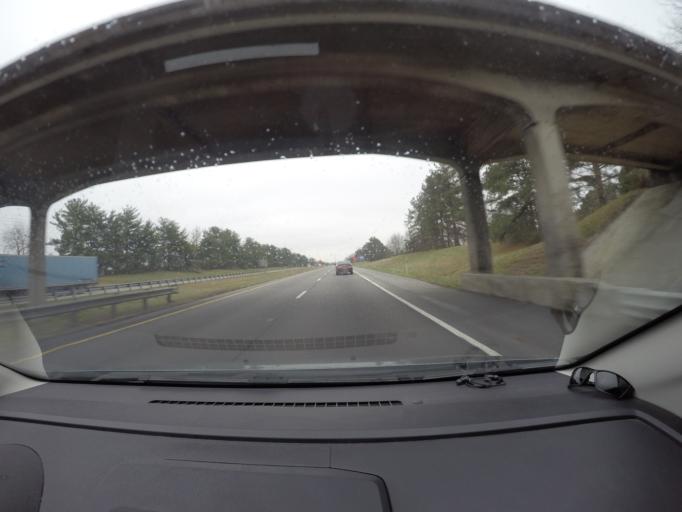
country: US
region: Tennessee
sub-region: Coffee County
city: Manchester
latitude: 35.4765
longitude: -86.0631
